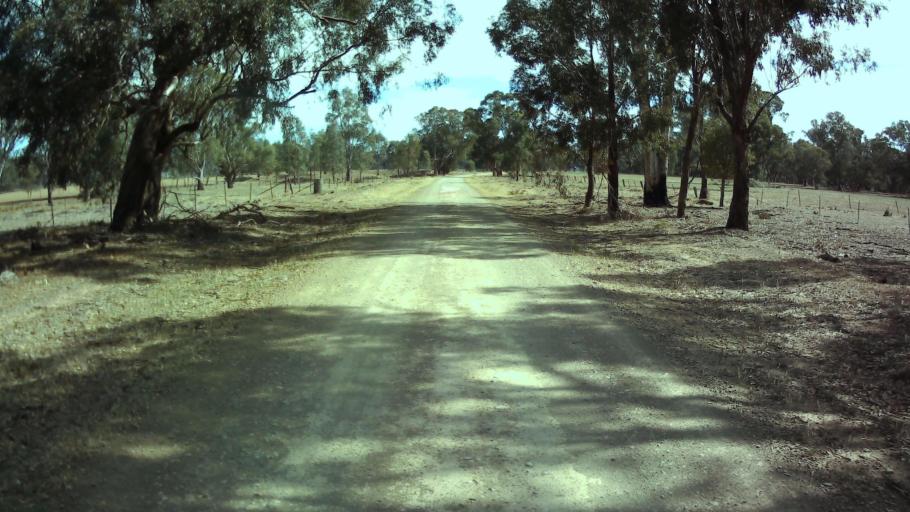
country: AU
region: New South Wales
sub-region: Weddin
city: Grenfell
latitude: -33.6927
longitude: 148.3036
